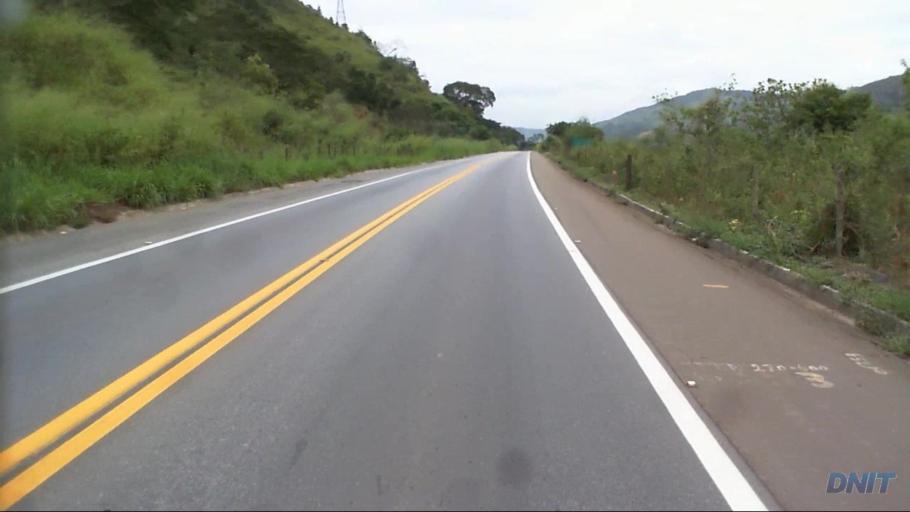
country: BR
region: Minas Gerais
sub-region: Timoteo
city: Timoteo
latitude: -19.5778
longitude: -42.7217
